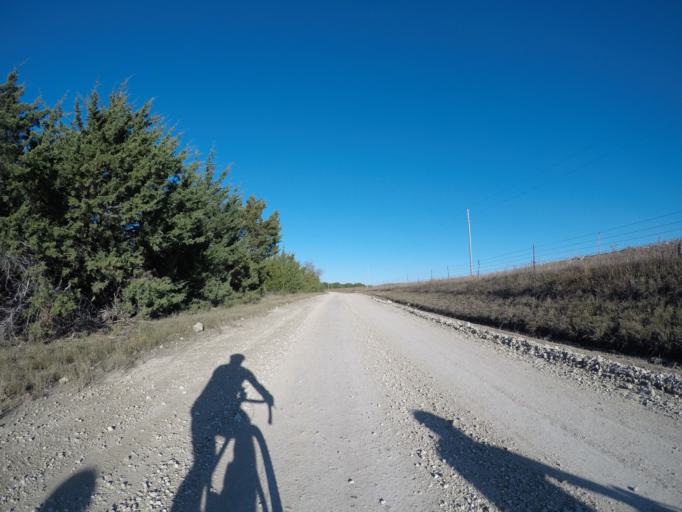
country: US
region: Kansas
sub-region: Wabaunsee County
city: Alma
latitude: 38.9289
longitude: -96.4716
